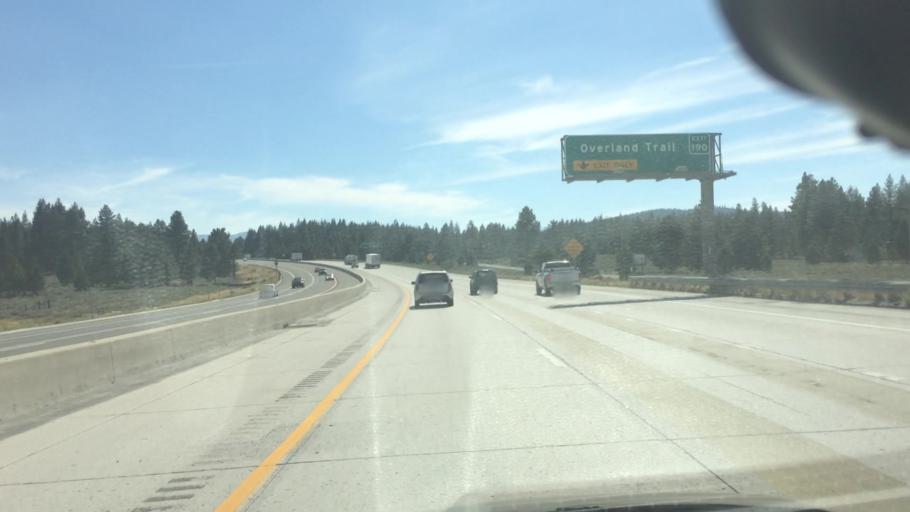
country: US
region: California
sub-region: Nevada County
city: Truckee
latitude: 39.3589
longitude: -120.1407
